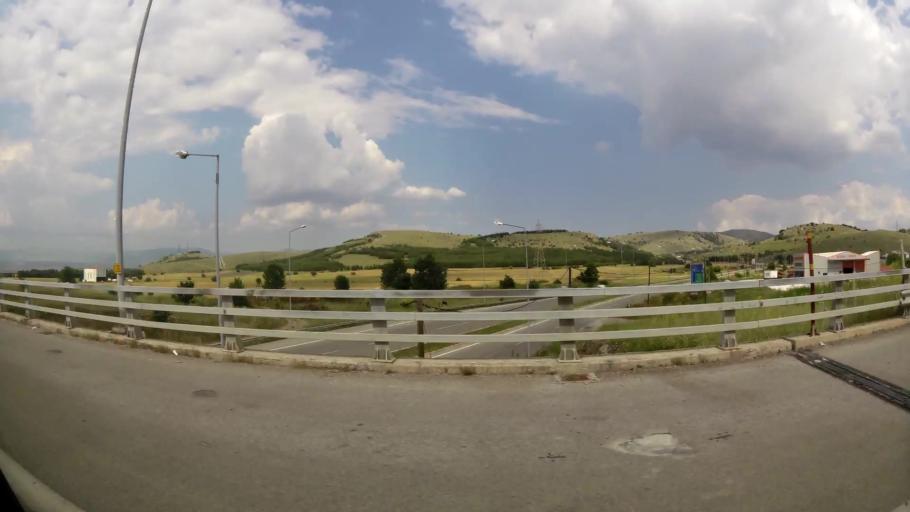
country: GR
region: West Macedonia
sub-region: Nomos Kozanis
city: Koila
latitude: 40.3437
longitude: 21.8064
